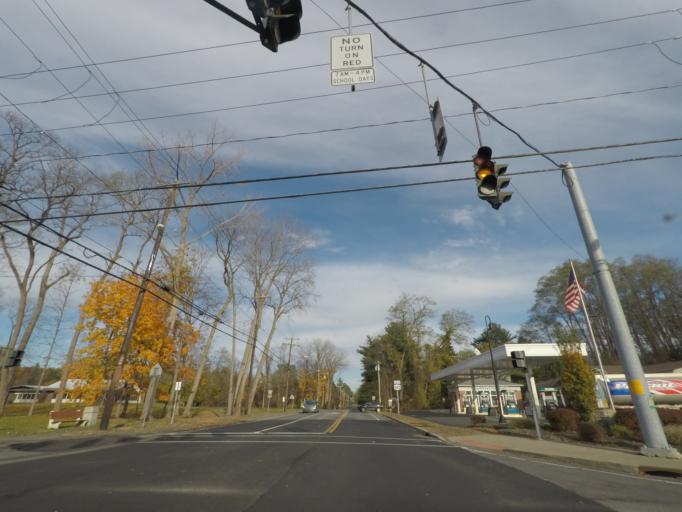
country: US
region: New York
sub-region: Albany County
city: Delmar
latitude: 42.6153
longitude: -73.8518
